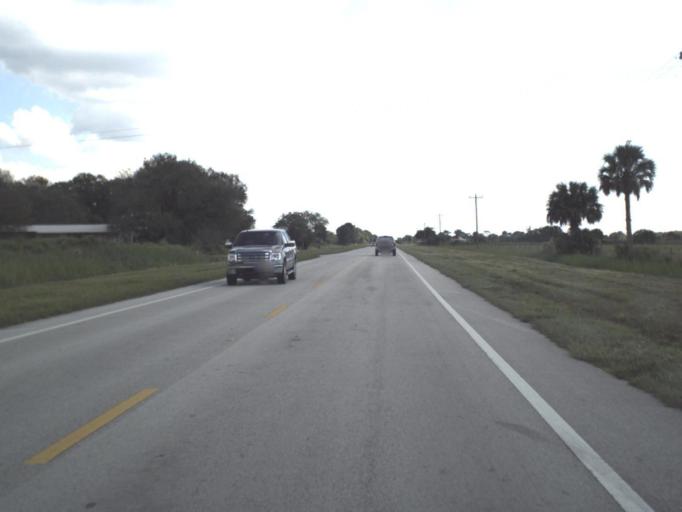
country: US
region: Florida
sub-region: Okeechobee County
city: Okeechobee
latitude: 27.3064
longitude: -80.9010
